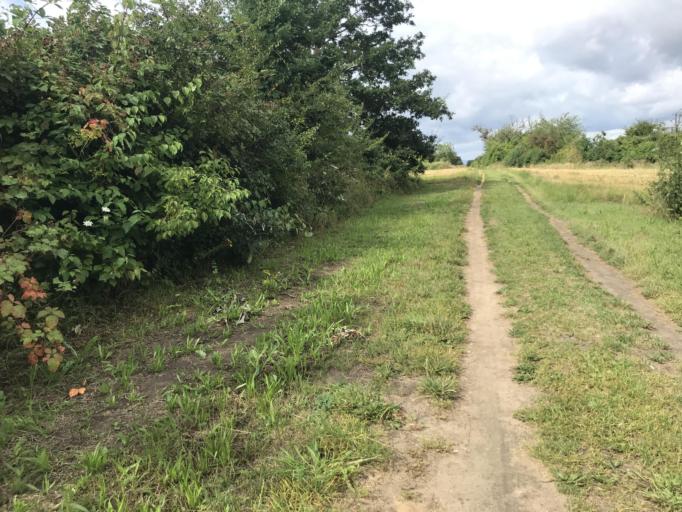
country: DE
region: Rheinland-Pfalz
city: Wackernheim
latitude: 49.9787
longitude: 8.1055
